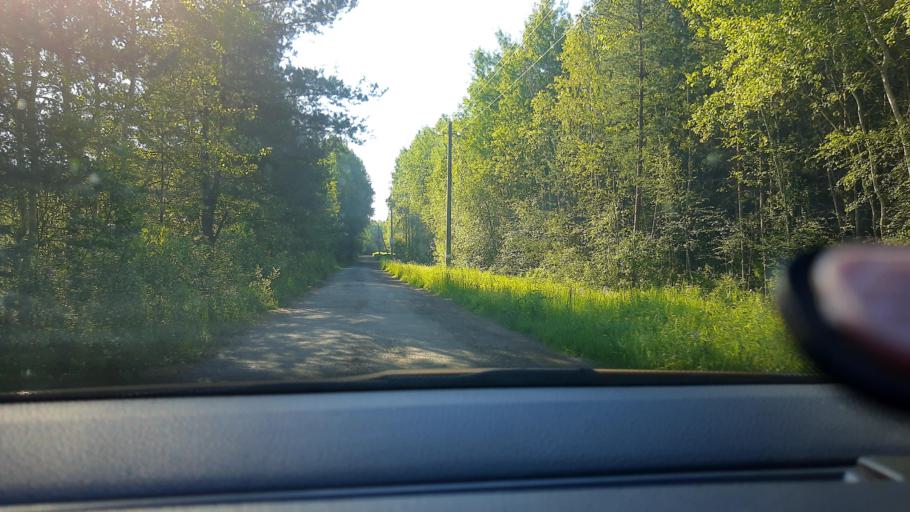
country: RU
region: Moskovskaya
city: Elektrogorsk
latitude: 55.8982
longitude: 38.7098
